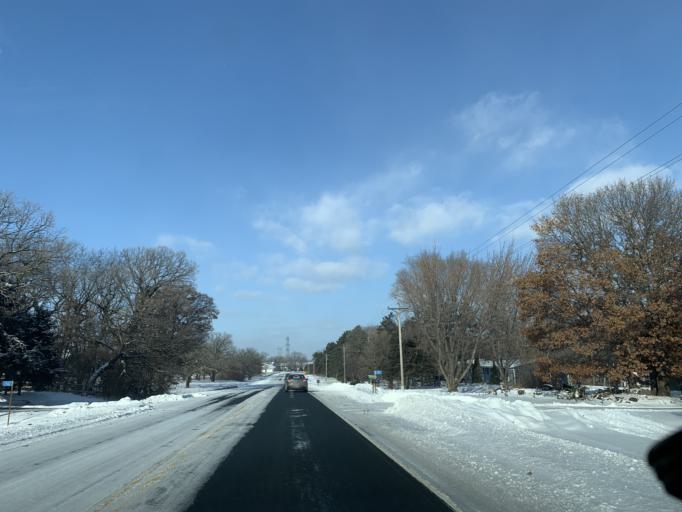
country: US
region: Minnesota
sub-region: Scott County
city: Prior Lake
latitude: 44.7708
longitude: -93.4056
